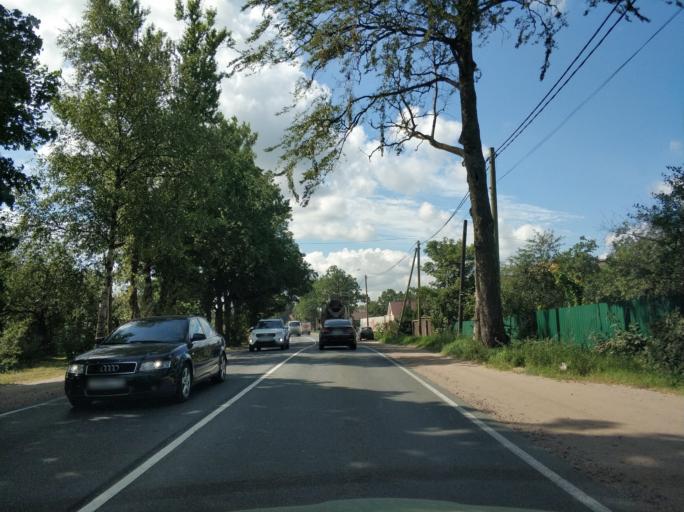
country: RU
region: Leningrad
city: Romanovka
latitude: 60.0459
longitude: 30.6972
